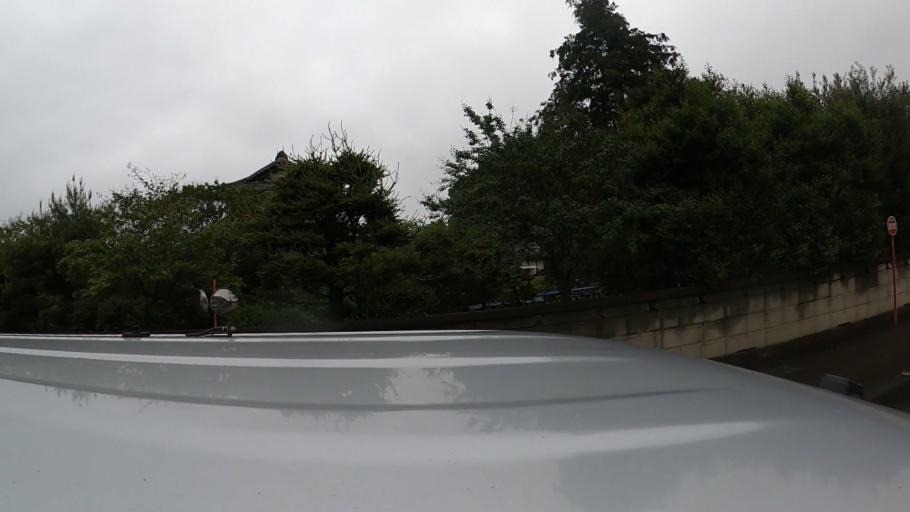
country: JP
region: Ibaraki
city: Ushiku
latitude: 36.0144
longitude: 140.1020
